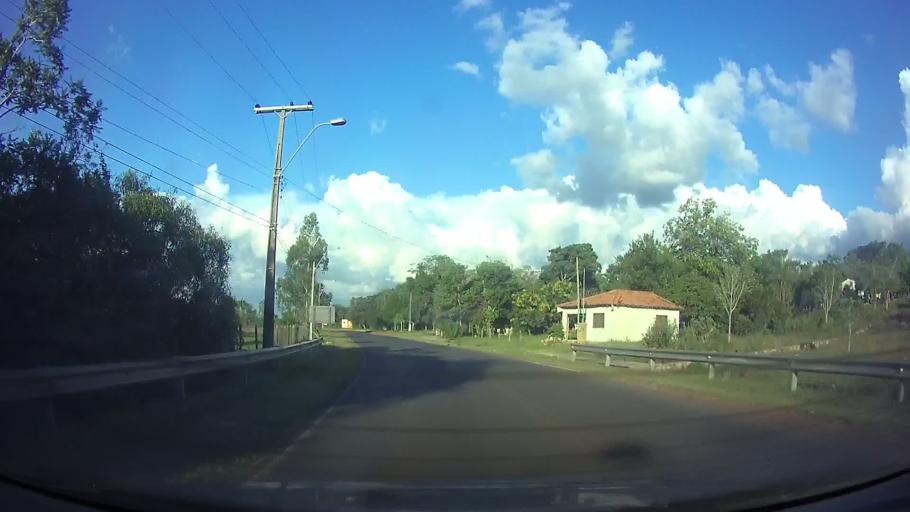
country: PY
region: Cordillera
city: Emboscada
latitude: -25.1857
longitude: -57.3001
